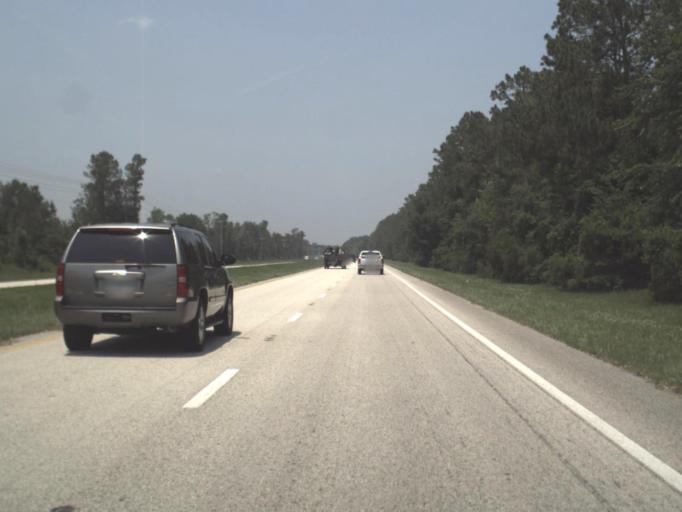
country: US
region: Florida
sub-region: Duval County
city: Baldwin
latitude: 30.1677
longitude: -82.0269
